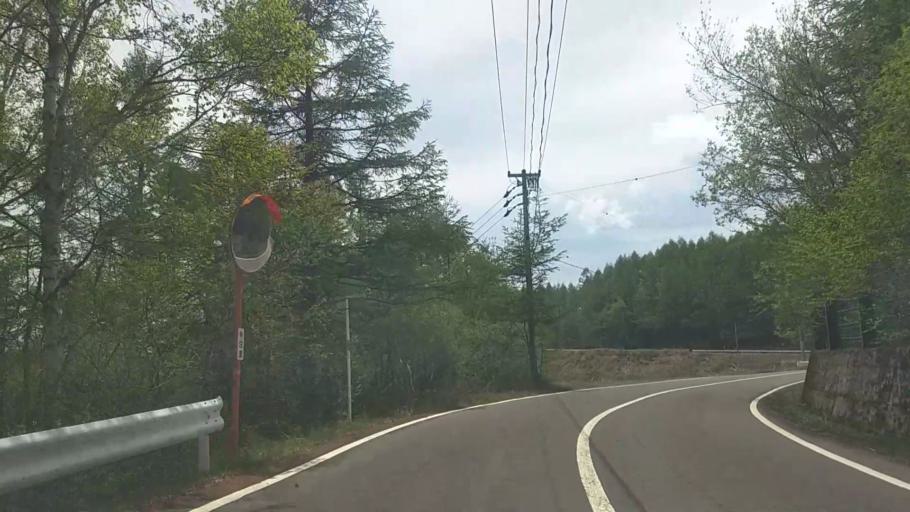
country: JP
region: Nagano
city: Saku
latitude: 36.0669
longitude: 138.3920
